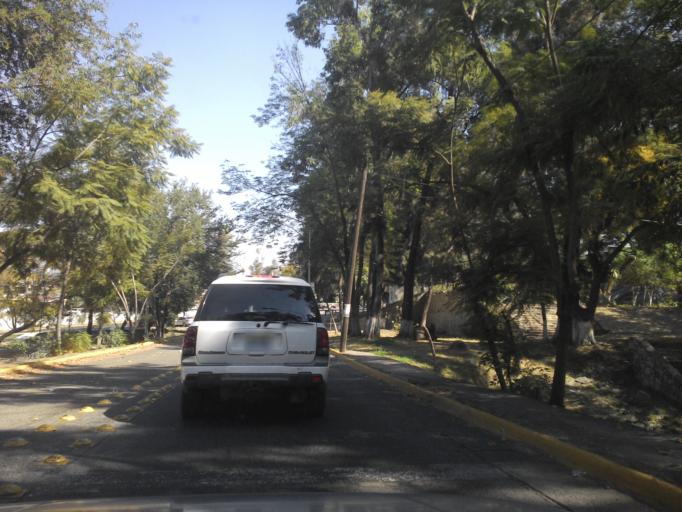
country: MX
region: Jalisco
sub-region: Zapopan
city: Zapopan
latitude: 20.7064
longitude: -103.3609
